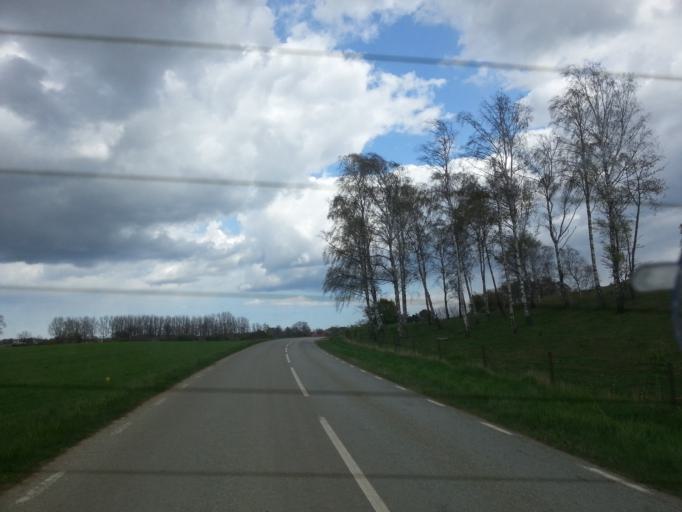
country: SE
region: Skane
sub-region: Ystads Kommun
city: Kopingebro
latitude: 55.3935
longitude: 14.1182
